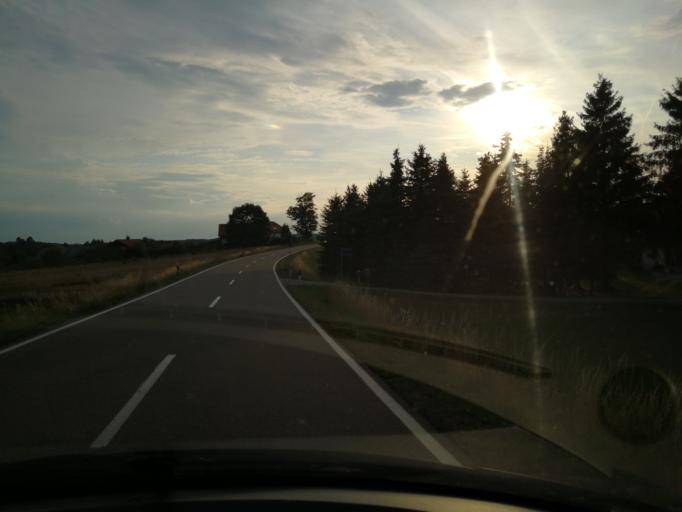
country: DE
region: Bavaria
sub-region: Lower Bavaria
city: Wiesenfelden
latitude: 49.0449
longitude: 12.5569
